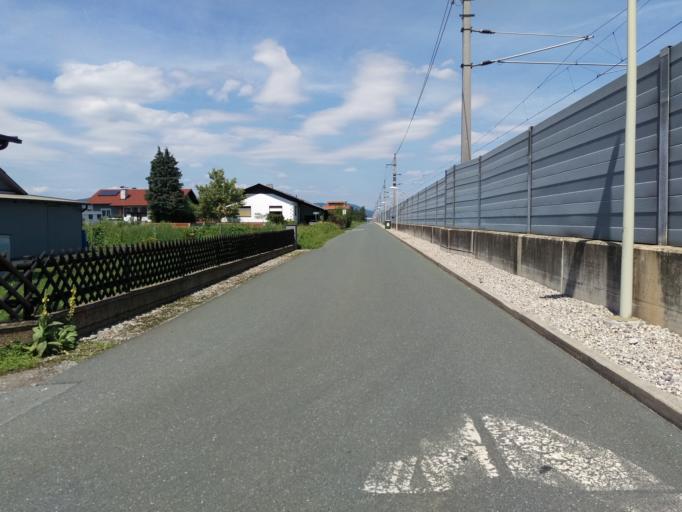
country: AT
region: Styria
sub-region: Politischer Bezirk Graz-Umgebung
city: Feldkirchen bei Graz
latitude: 46.9895
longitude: 15.4545
